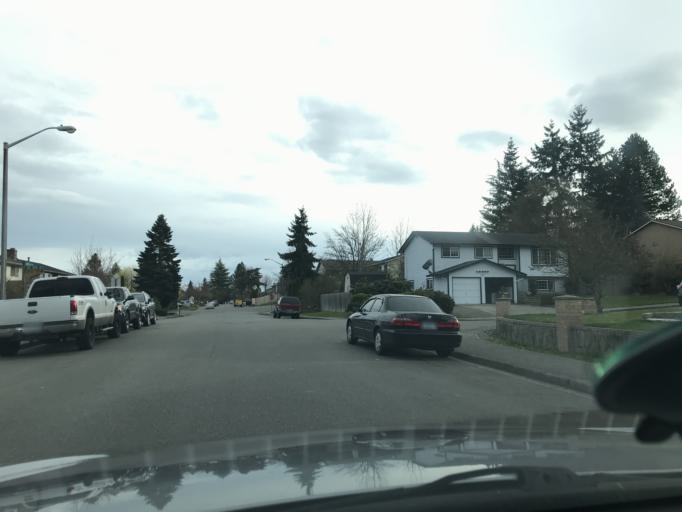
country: US
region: Washington
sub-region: King County
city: East Hill-Meridian
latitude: 47.4096
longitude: -122.1712
